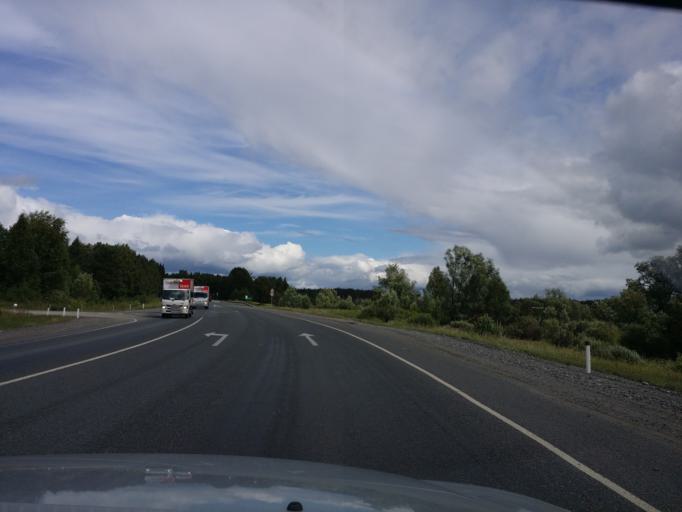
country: RU
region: Tjumen
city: Tobol'sk
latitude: 58.3013
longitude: 68.3311
